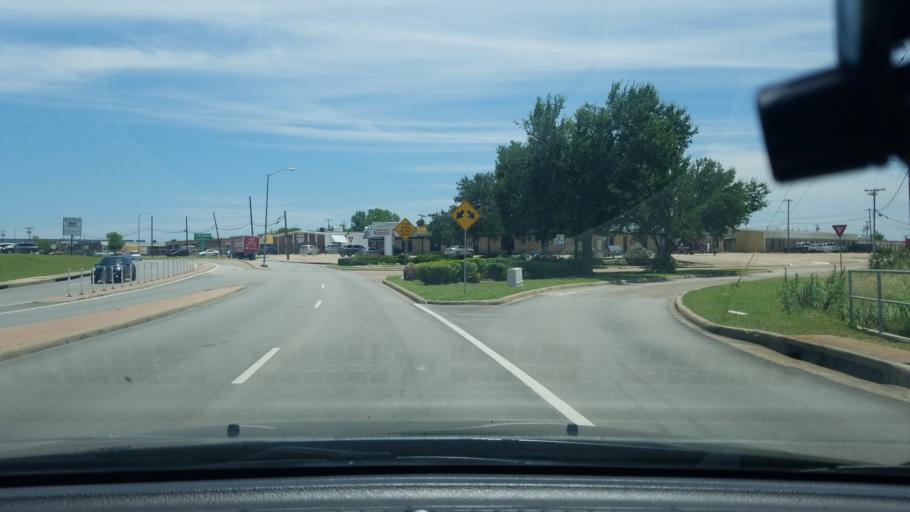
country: US
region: Texas
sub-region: Dallas County
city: Mesquite
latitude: 32.7714
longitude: -96.6130
